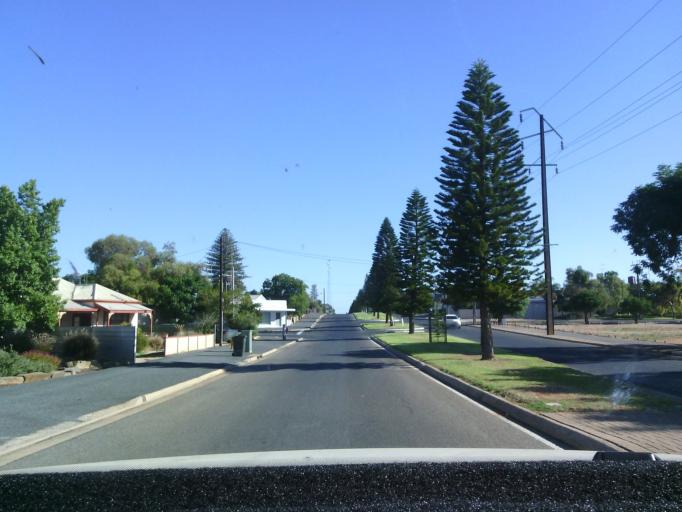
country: AU
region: South Australia
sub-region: Berri and Barmera
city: Berri
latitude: -34.2796
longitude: 140.5973
